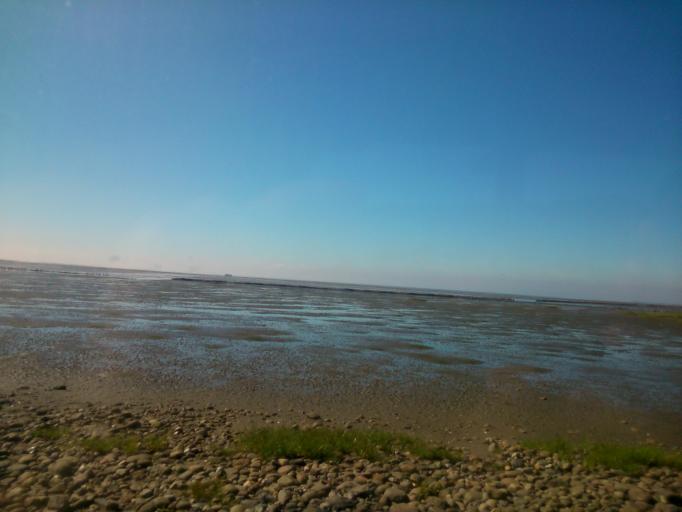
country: DK
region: South Denmark
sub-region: Esbjerg Kommune
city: Ribe
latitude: 55.3097
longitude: 8.6442
